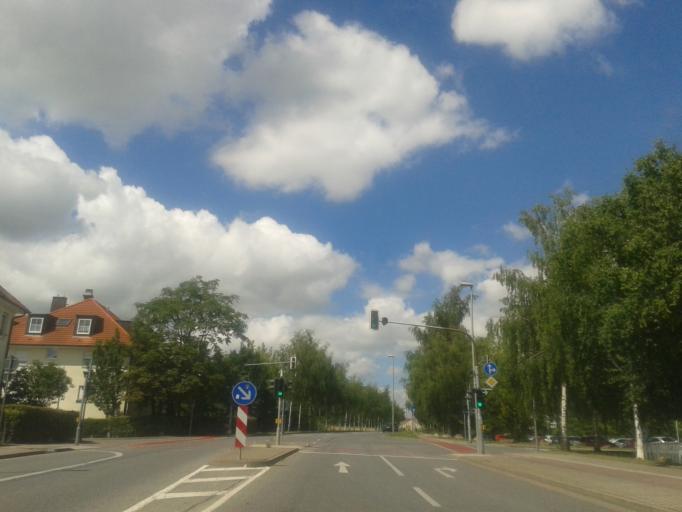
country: DE
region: Saxony
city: Dresden
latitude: 51.0191
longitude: 13.7358
